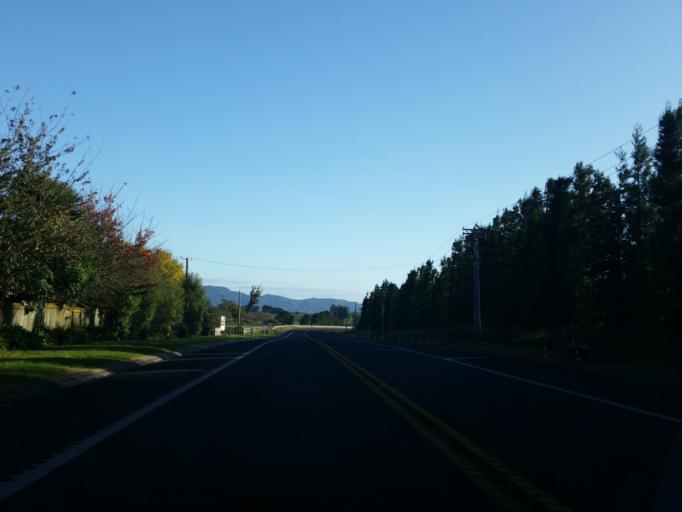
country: NZ
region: Bay of Plenty
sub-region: Western Bay of Plenty District
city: Katikati
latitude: -37.6234
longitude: 175.9534
